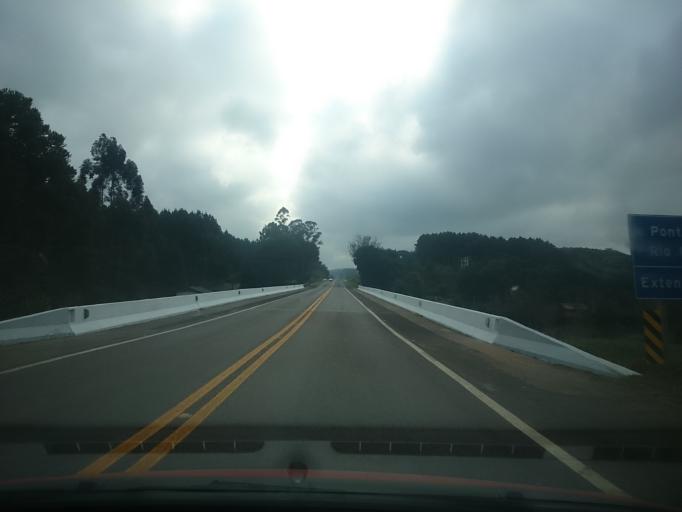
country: BR
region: Santa Catarina
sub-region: Lages
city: Lages
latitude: -27.8759
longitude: -50.4042
